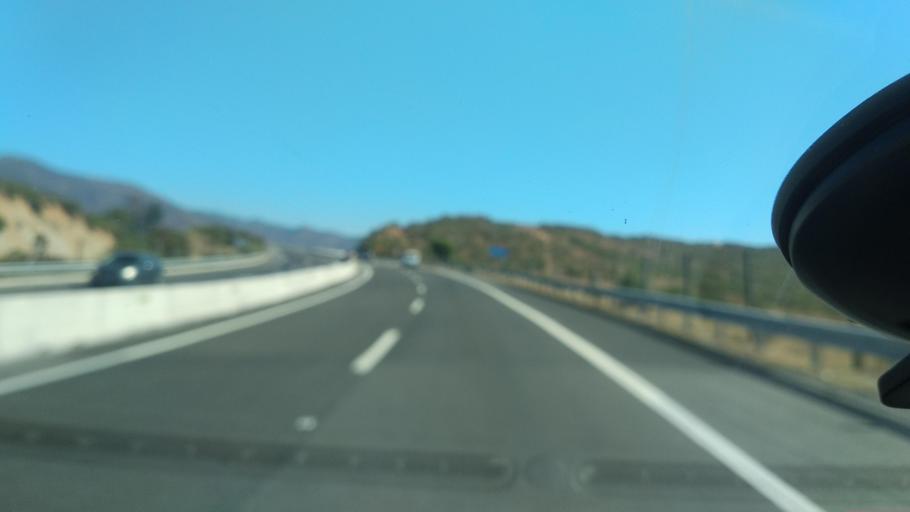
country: CL
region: Valparaiso
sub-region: Provincia de Marga Marga
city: Villa Alemana
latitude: -33.0312
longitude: -71.3201
